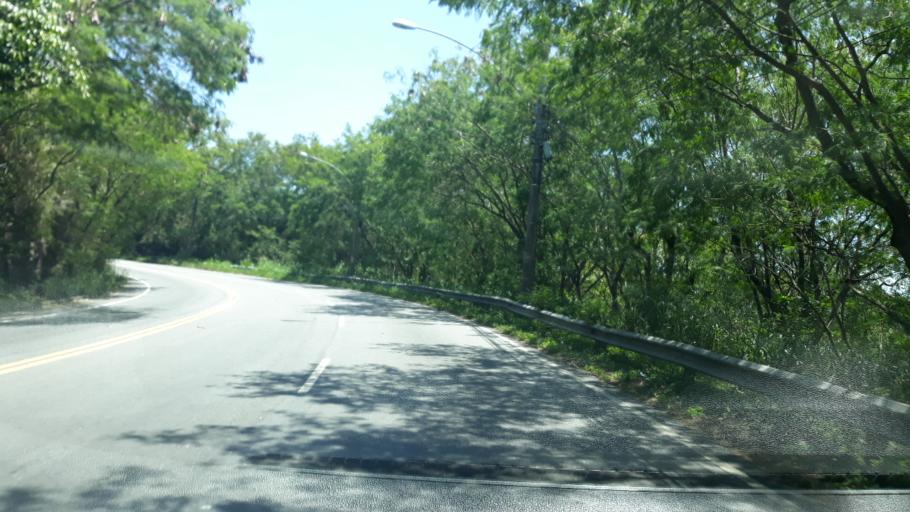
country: BR
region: Rio de Janeiro
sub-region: Nilopolis
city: Nilopolis
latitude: -23.0082
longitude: -43.5132
